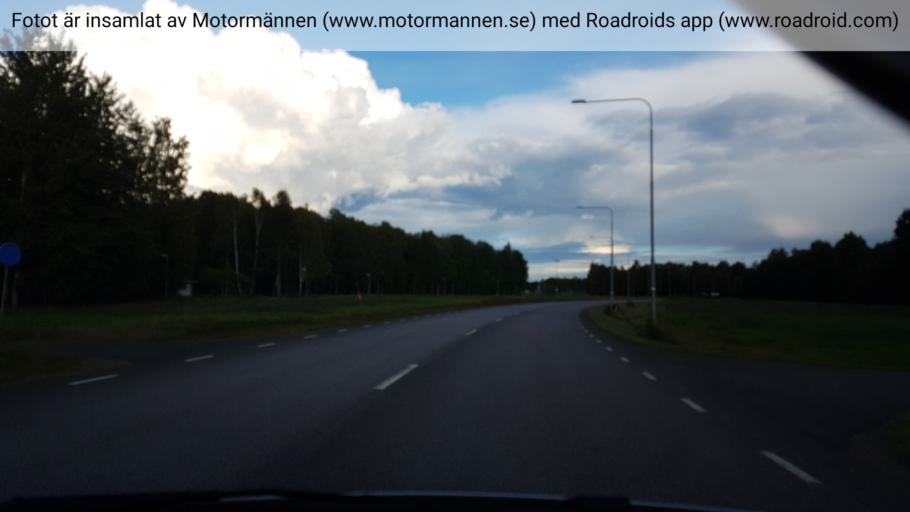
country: SE
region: Vaestra Goetaland
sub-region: Tibro Kommun
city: Tibro
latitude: 58.4135
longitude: 14.1617
